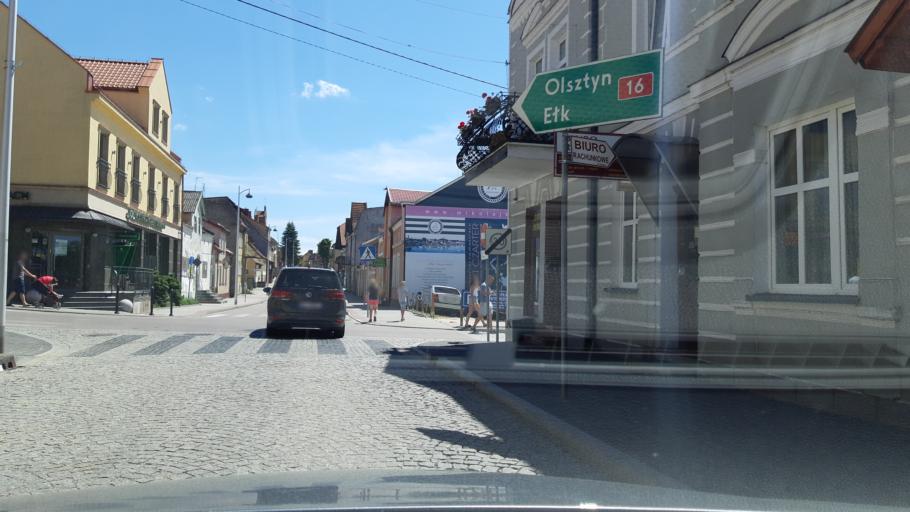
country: PL
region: Warmian-Masurian Voivodeship
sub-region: Powiat mragowski
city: Mikolajki
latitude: 53.8000
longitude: 21.5739
